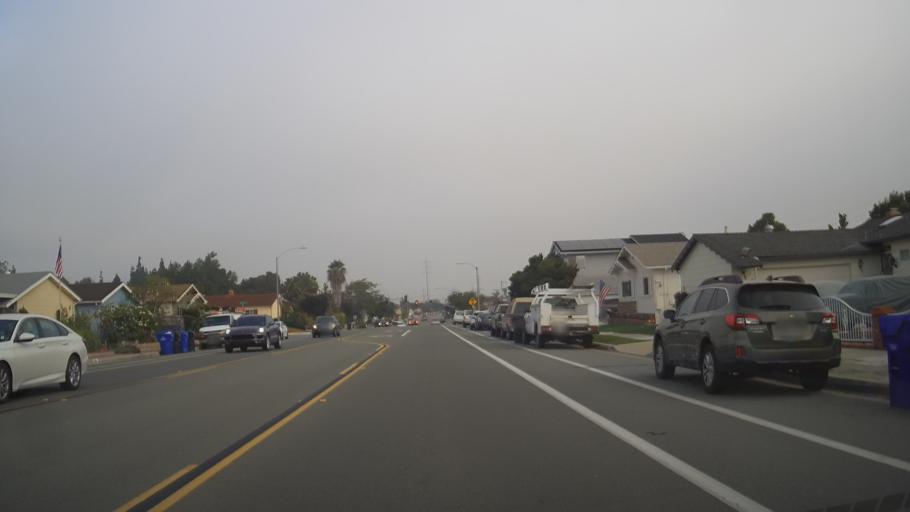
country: US
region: California
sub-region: San Diego County
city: San Diego
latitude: 32.7880
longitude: -117.1448
